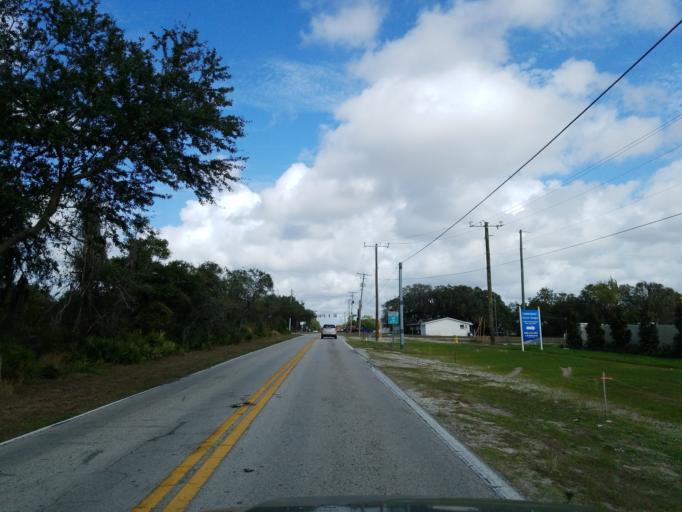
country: US
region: Florida
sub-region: Hillsborough County
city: Valrico
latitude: 27.9357
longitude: -82.2196
